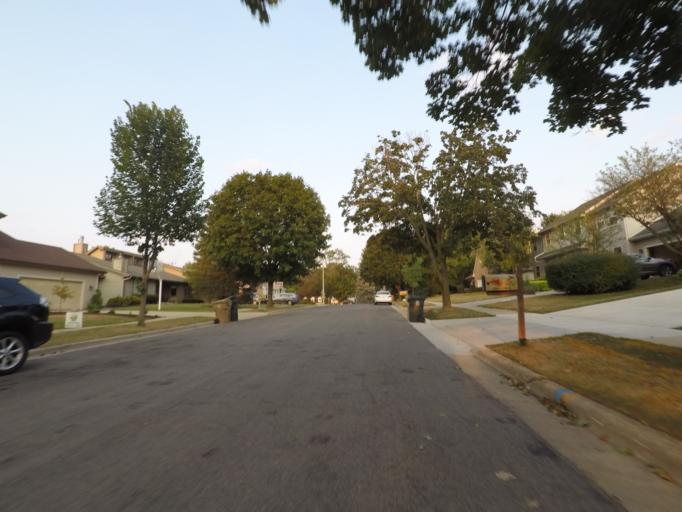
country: US
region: Wisconsin
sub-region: Dane County
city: Middleton
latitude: 43.0682
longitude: -89.5157
